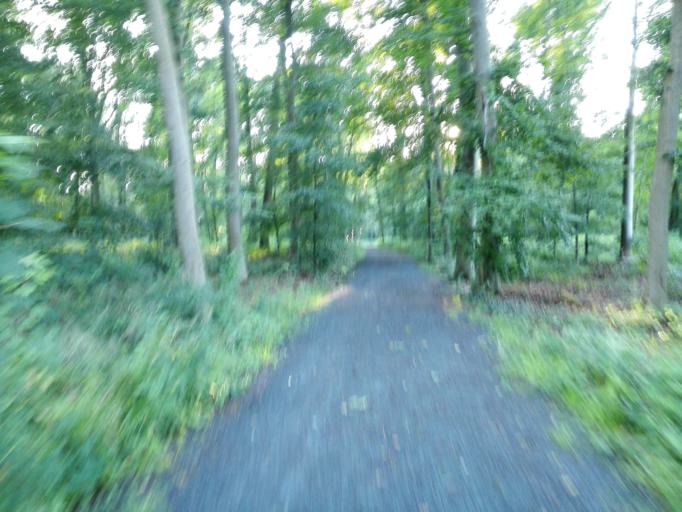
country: BE
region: Flanders
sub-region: Provincie Vlaams-Brabant
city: Oud-Heverlee
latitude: 50.8194
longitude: 4.7004
